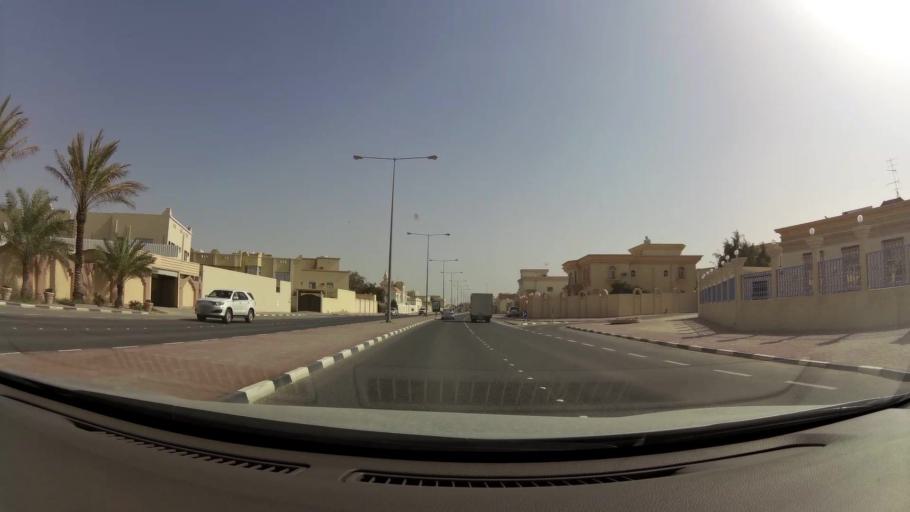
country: QA
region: Baladiyat Umm Salal
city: Umm Salal Muhammad
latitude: 25.3687
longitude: 51.4352
